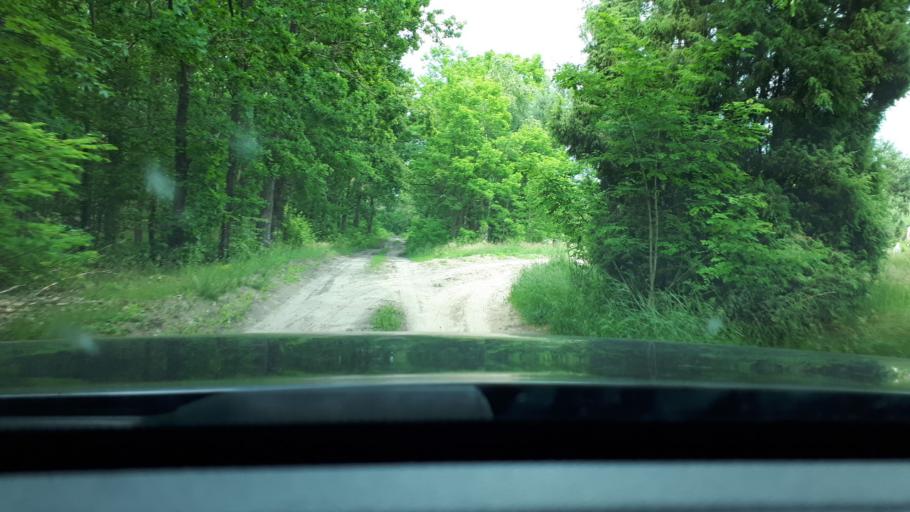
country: PL
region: Masovian Voivodeship
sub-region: Powiat warszawski zachodni
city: Kampinos
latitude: 52.2699
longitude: 20.5132
